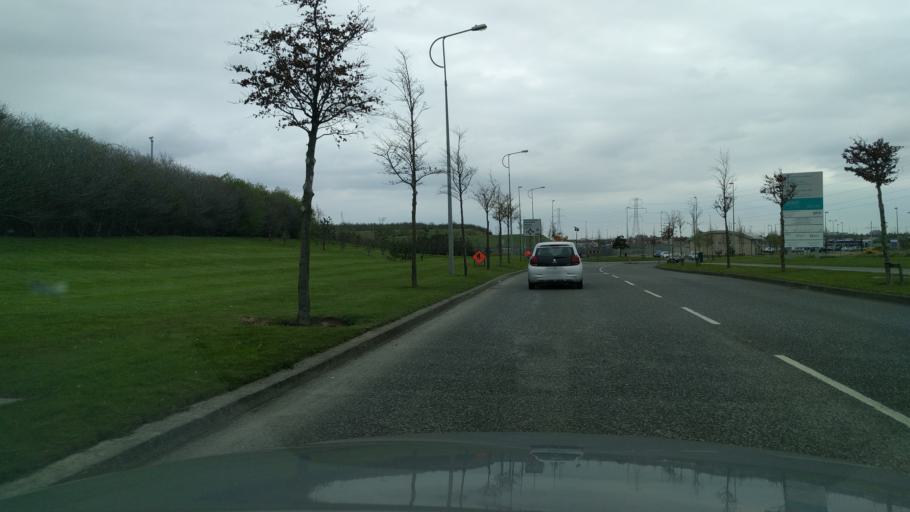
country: IE
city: Jobstown
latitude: 53.2912
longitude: -6.4116
